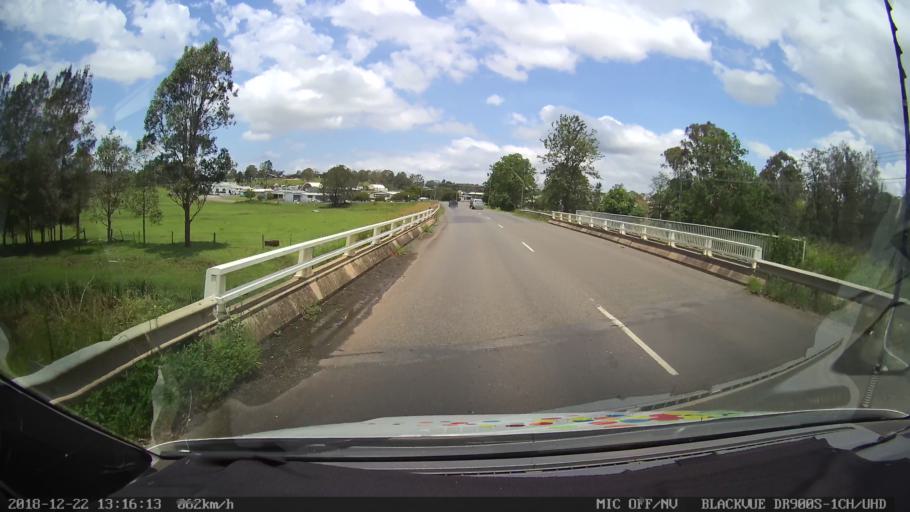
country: AU
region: New South Wales
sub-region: Clarence Valley
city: South Grafton
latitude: -29.7243
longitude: 152.9388
